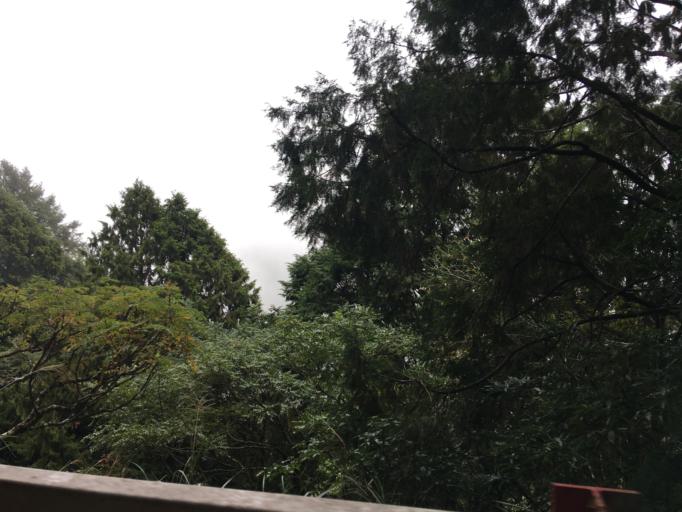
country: TW
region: Taiwan
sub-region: Yilan
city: Yilan
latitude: 24.4839
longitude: 121.5355
